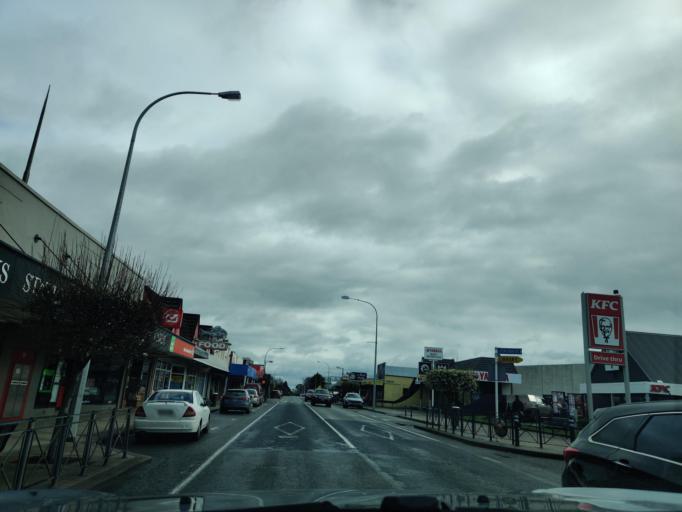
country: NZ
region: Manawatu-Wanganui
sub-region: Palmerston North City
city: Palmerston North
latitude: -40.2096
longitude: 176.0968
